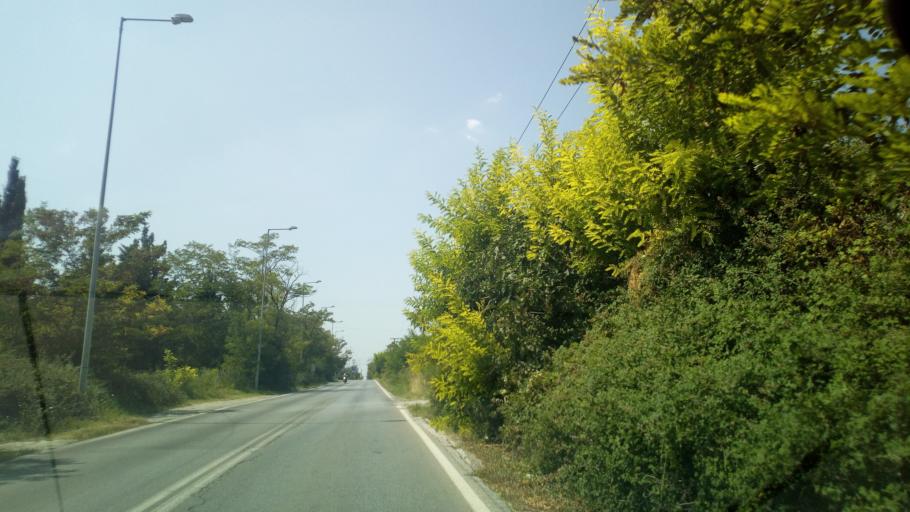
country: GR
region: Central Macedonia
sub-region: Nomos Thessalonikis
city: Chortiatis
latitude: 40.6252
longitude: 23.0679
